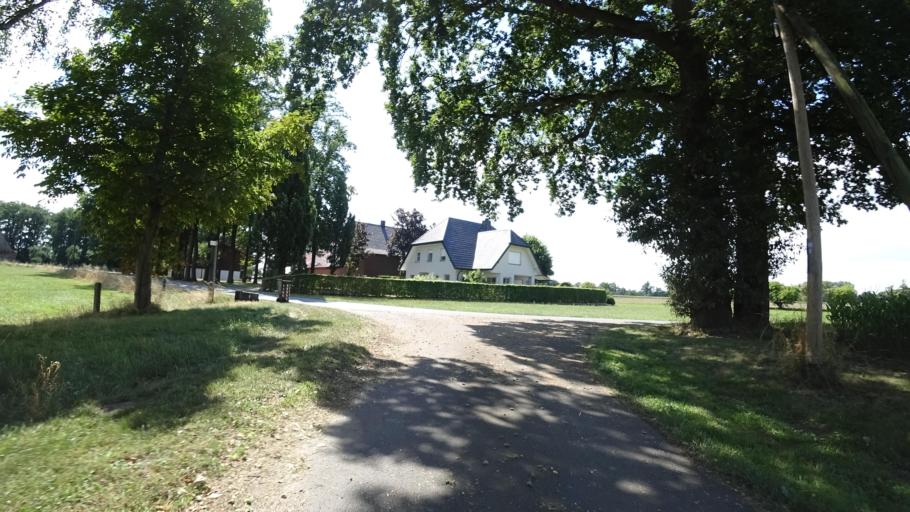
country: DE
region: North Rhine-Westphalia
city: Rietberg
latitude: 51.8685
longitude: 8.4462
